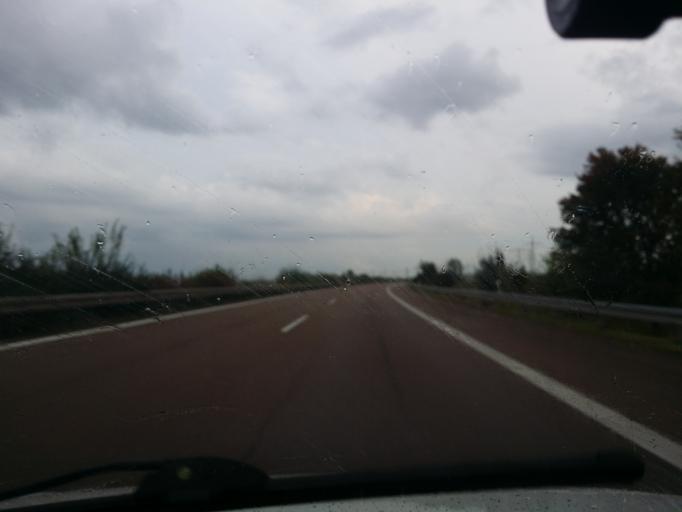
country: DE
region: Saxony-Anhalt
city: Beuna
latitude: 51.2944
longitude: 11.9736
